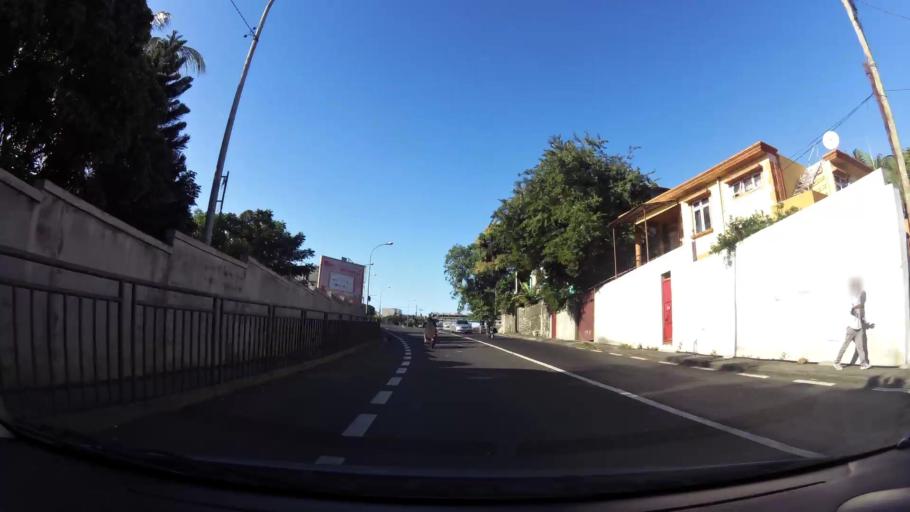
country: MU
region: Moka
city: Pailles
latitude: -20.1719
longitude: 57.4773
